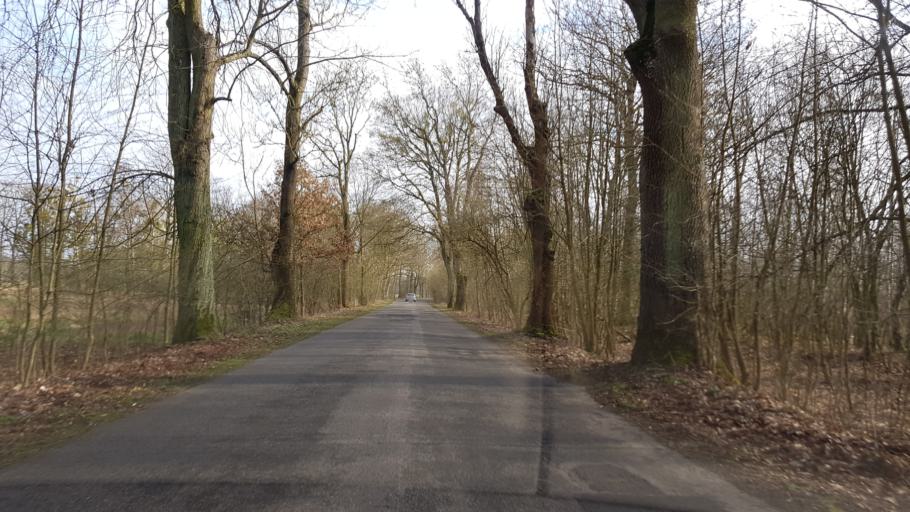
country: PL
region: West Pomeranian Voivodeship
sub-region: Powiat policki
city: Dobra
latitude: 53.5379
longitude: 14.3181
